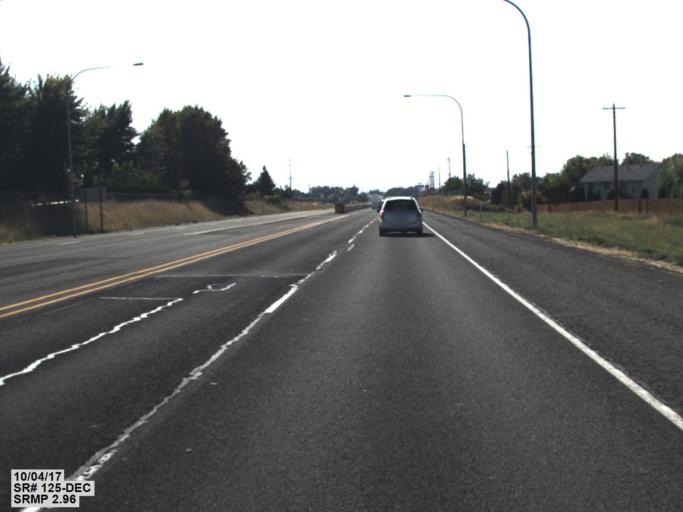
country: US
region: Washington
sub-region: Walla Walla County
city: College Place
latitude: 46.0375
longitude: -118.3704
